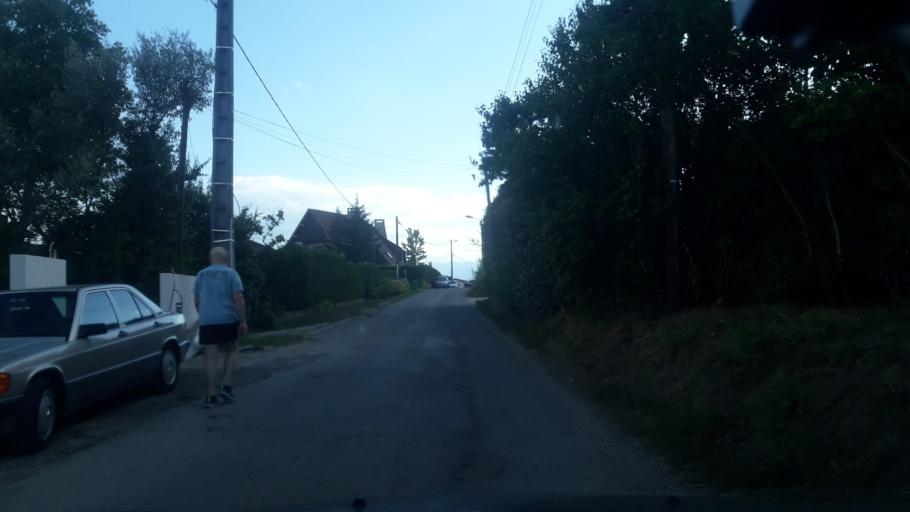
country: FR
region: Rhone-Alpes
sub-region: Departement de l'Isere
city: Saint-Ismier
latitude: 45.2426
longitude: 5.8133
